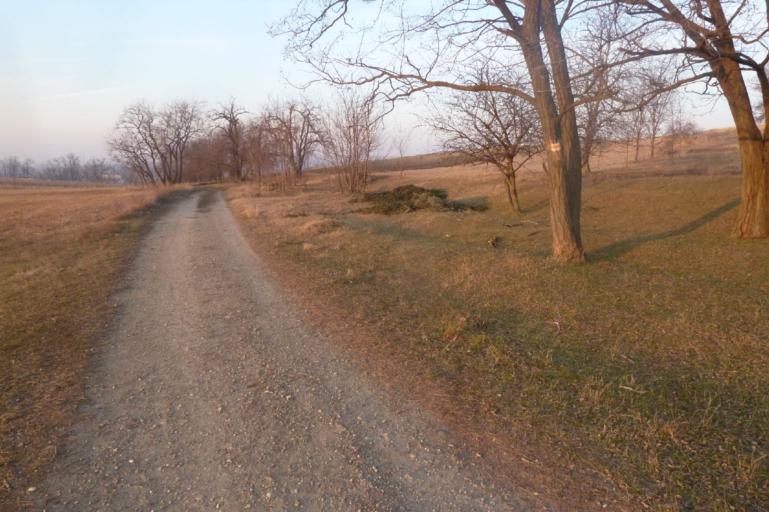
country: HU
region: Pest
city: Nagytarcsa
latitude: 47.5213
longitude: 19.3014
